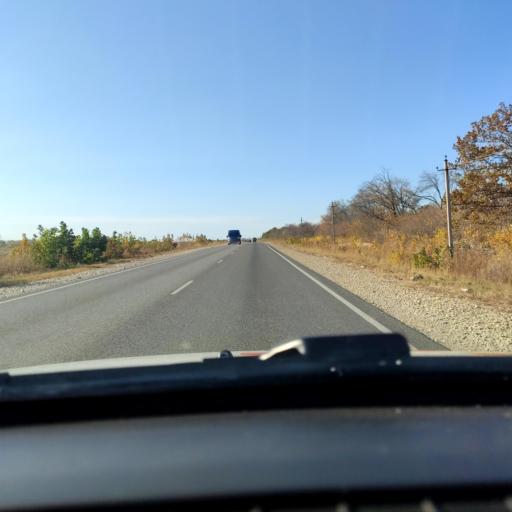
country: RU
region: Voronezj
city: Semiluki
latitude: 51.7293
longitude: 38.9808
